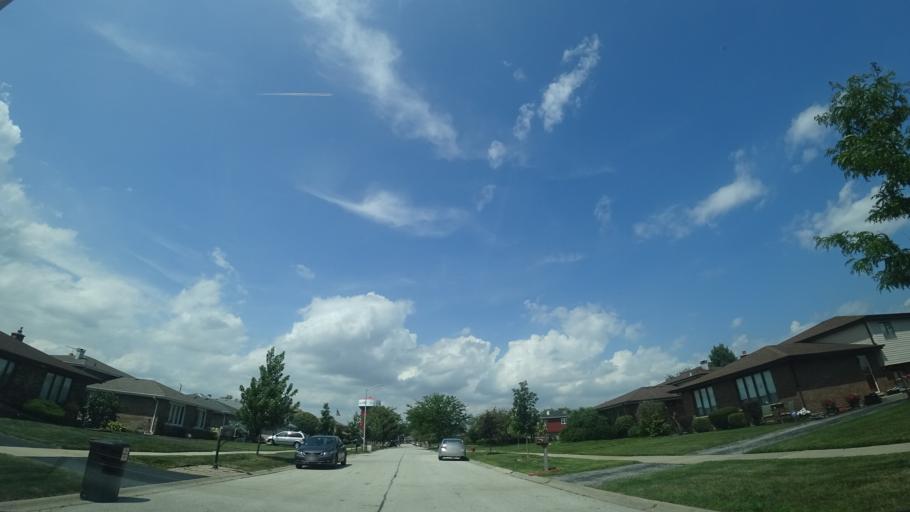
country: US
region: Illinois
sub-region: Cook County
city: Crestwood
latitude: 41.6729
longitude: -87.7518
